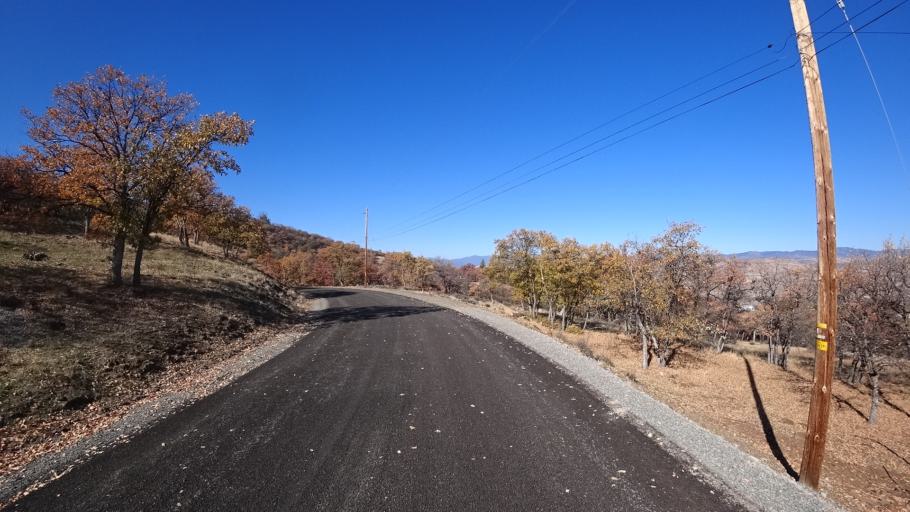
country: US
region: California
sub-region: Siskiyou County
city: Montague
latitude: 41.8771
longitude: -122.4904
